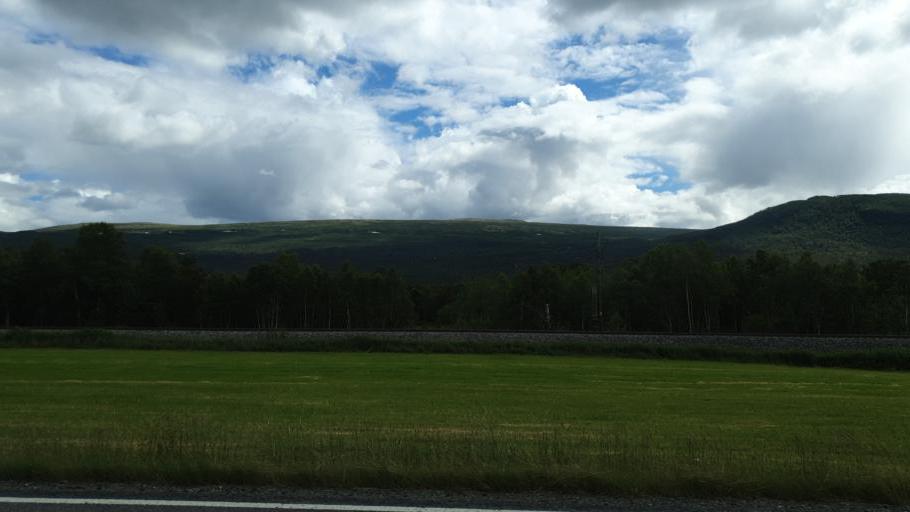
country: NO
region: Sor-Trondelag
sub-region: Oppdal
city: Oppdal
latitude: 62.6031
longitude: 9.7270
